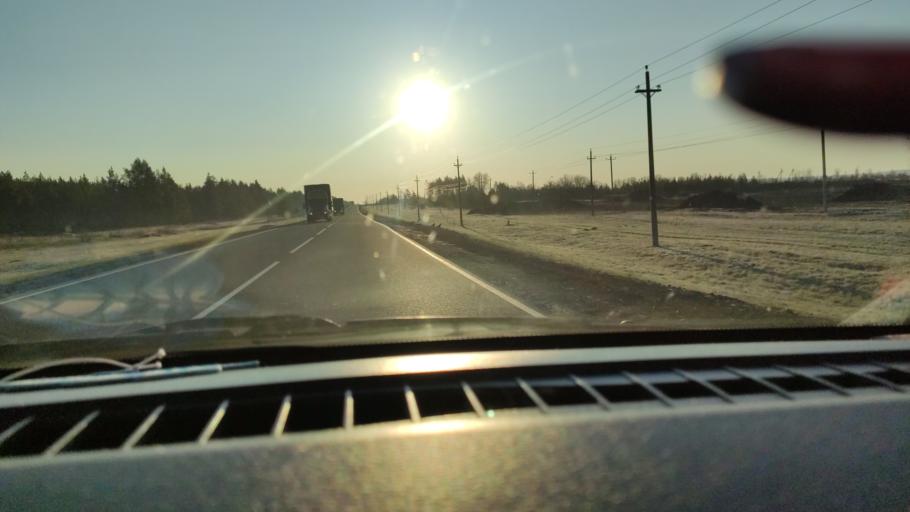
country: RU
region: Saratov
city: Sennoy
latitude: 52.1423
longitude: 46.9157
